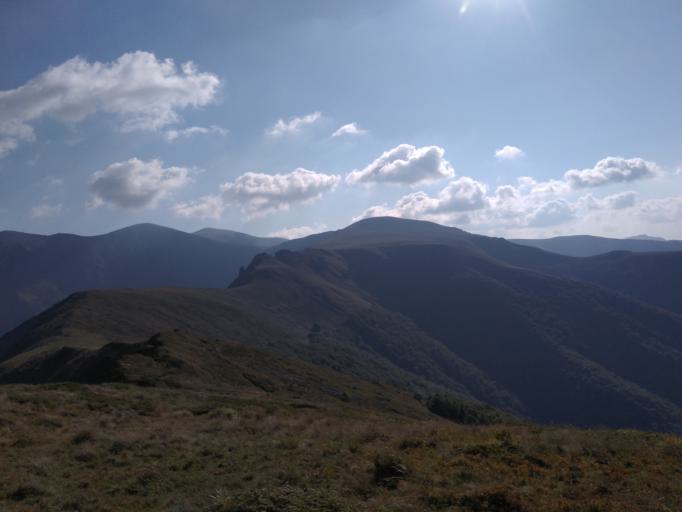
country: BG
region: Stara Zagora
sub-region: Obshtina Pavel Banya
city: Asen
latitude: 42.7604
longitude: 25.1030
